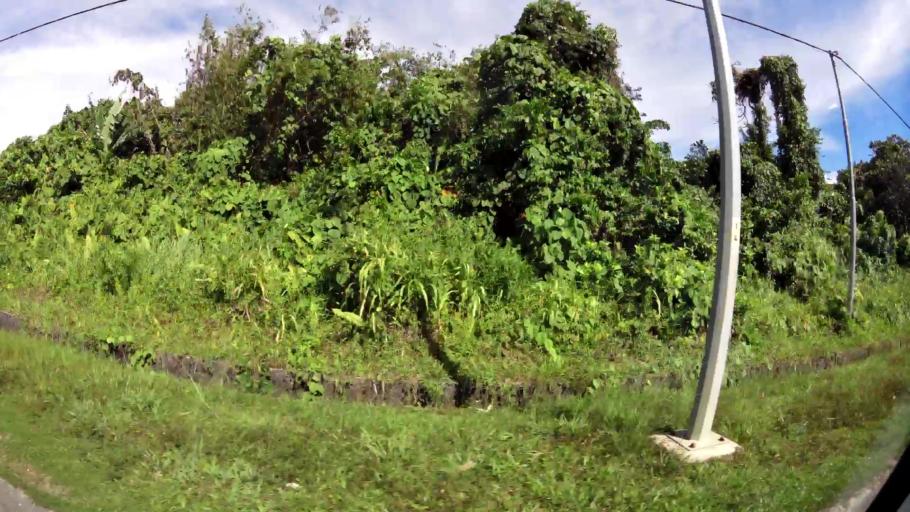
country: BN
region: Brunei and Muara
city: Bandar Seri Begawan
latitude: 5.0295
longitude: 115.0508
